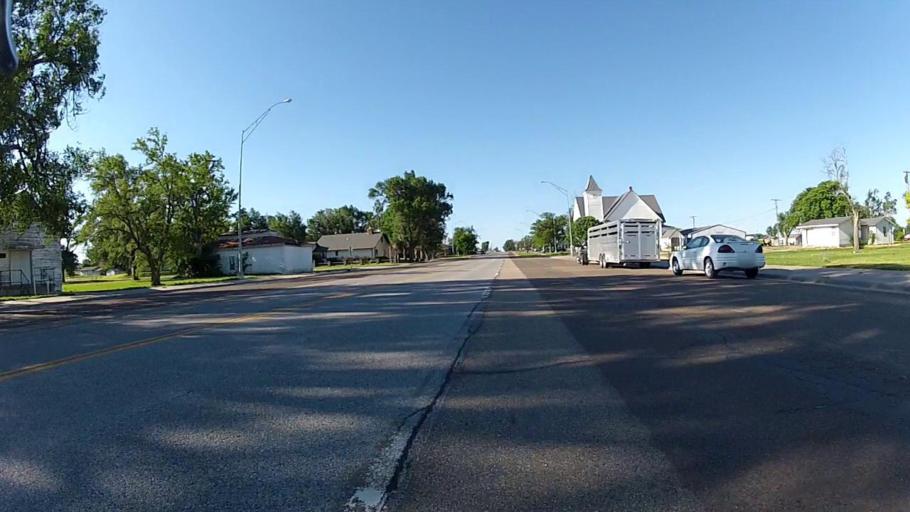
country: US
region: Kansas
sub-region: Ford County
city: Dodge City
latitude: 37.6381
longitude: -99.7539
